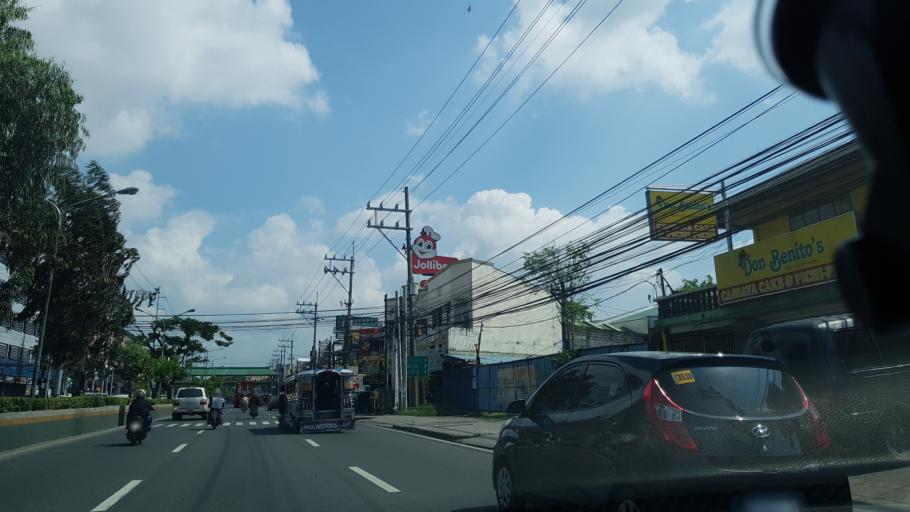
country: PH
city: Sambayanihan People's Village
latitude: 14.4802
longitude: 120.9972
